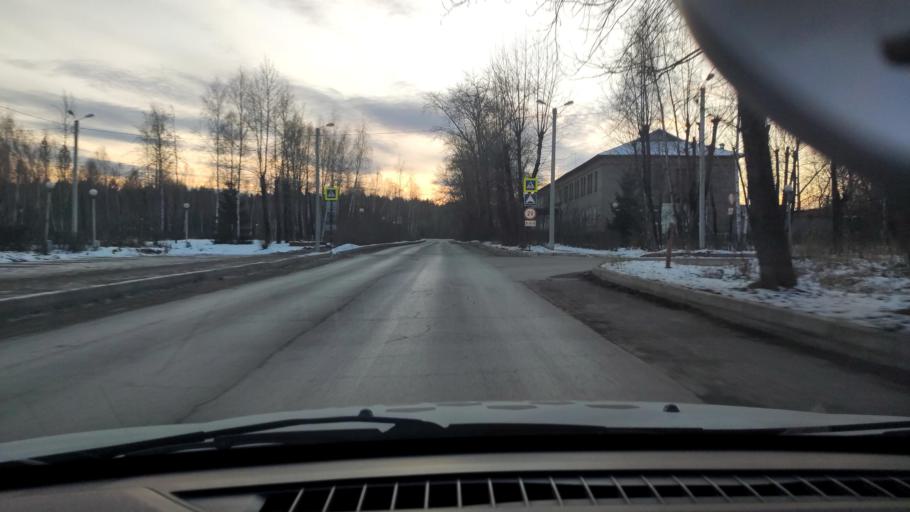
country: RU
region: Perm
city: Overyata
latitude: 58.0167
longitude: 55.9091
